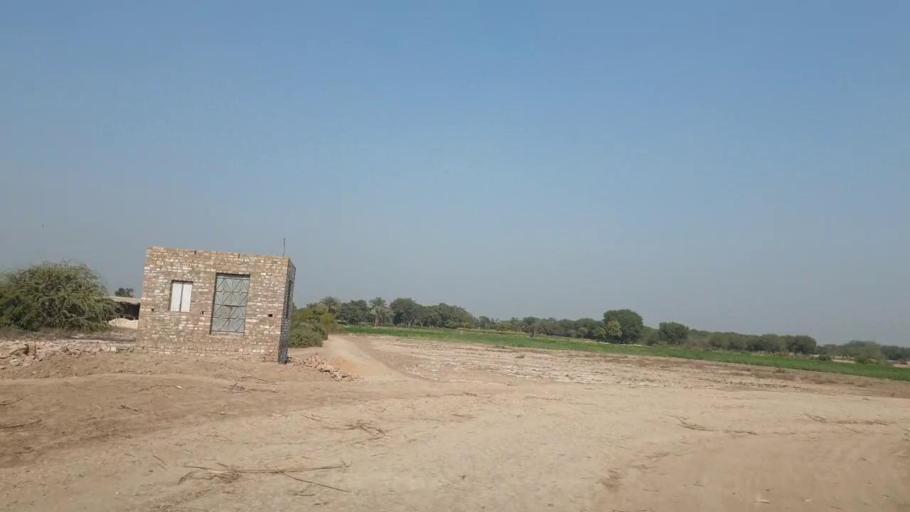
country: PK
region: Sindh
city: Tando Allahyar
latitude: 25.5498
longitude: 68.7141
